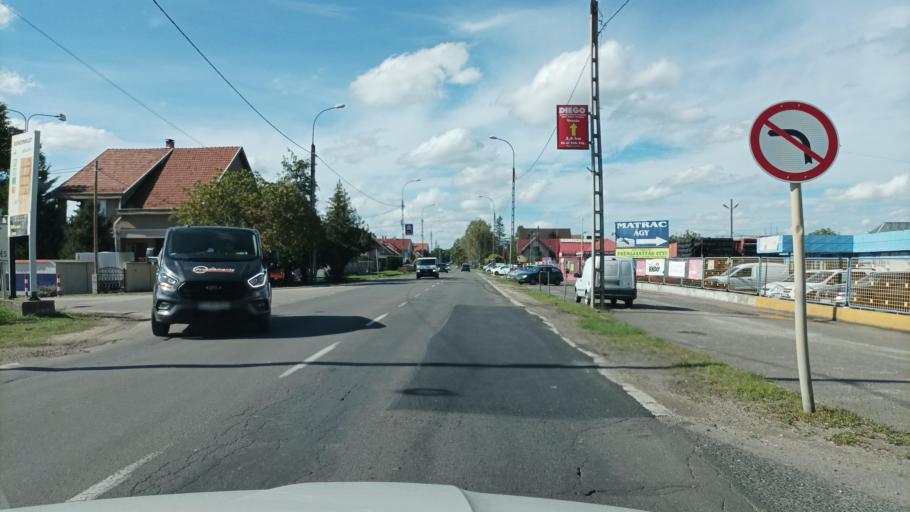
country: HU
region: Pest
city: Vecses
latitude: 47.4039
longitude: 19.2899
